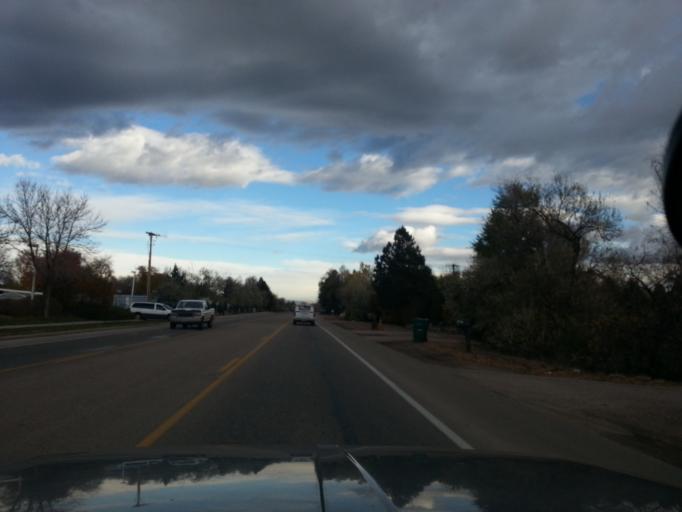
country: US
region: Colorado
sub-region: Larimer County
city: Fort Collins
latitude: 40.5339
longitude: -105.1152
